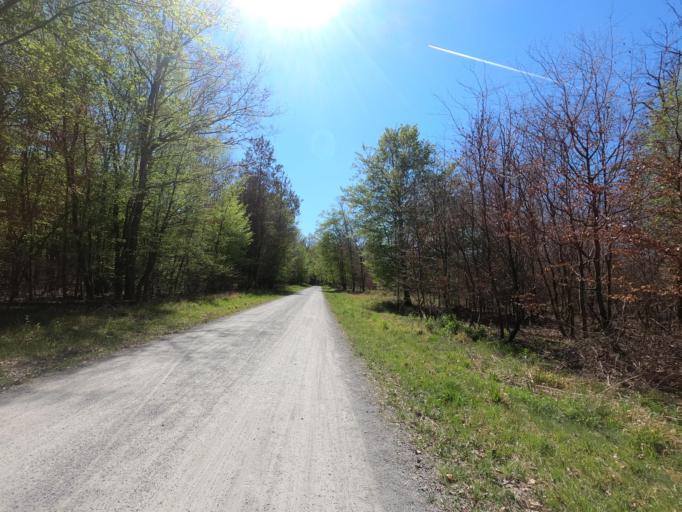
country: DE
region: Hesse
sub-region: Regierungsbezirk Darmstadt
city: Nauheim
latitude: 49.9623
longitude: 8.5047
